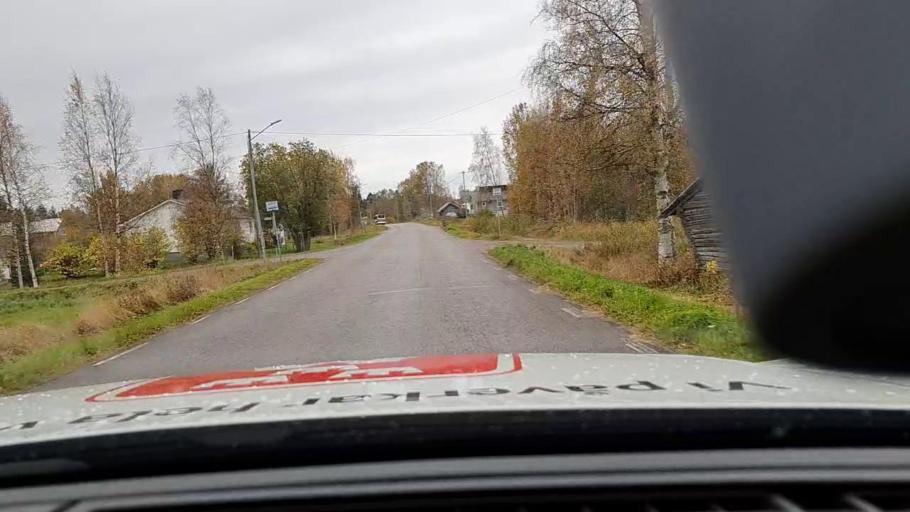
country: SE
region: Norrbotten
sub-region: Haparanda Kommun
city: Haparanda
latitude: 65.7986
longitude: 23.9198
